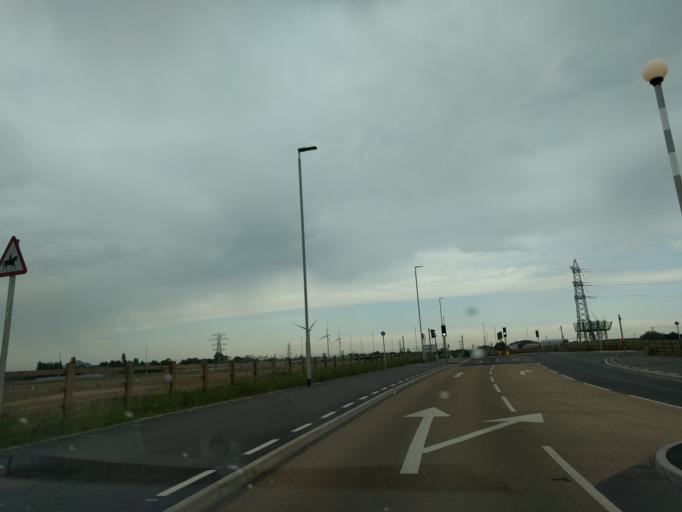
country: GB
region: England
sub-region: Nottinghamshire
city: Newark on Trent
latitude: 53.0544
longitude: -0.8061
